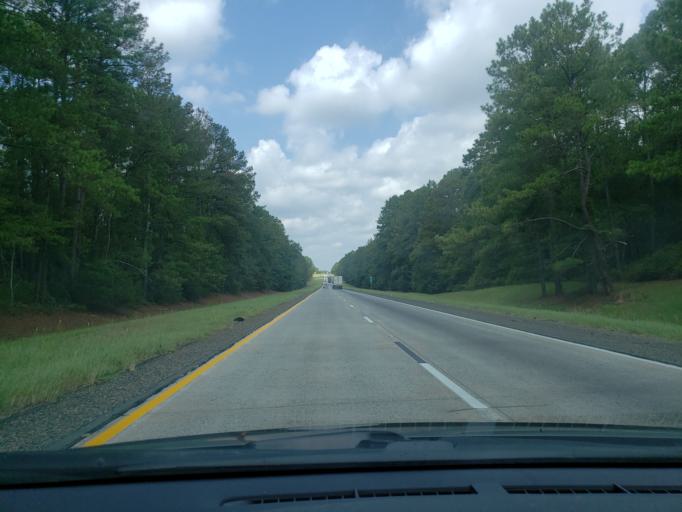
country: US
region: Georgia
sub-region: Treutlen County
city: Soperton
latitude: 32.4283
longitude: -82.5614
